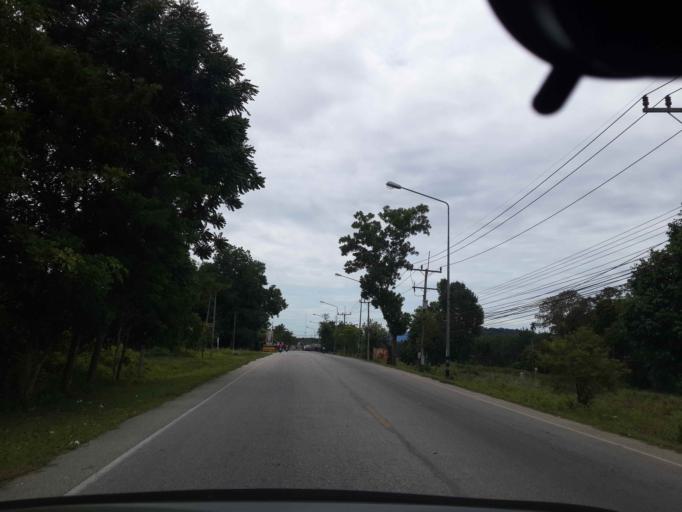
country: TH
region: Narathiwat
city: Yi-ngo
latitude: 6.3403
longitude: 101.6314
